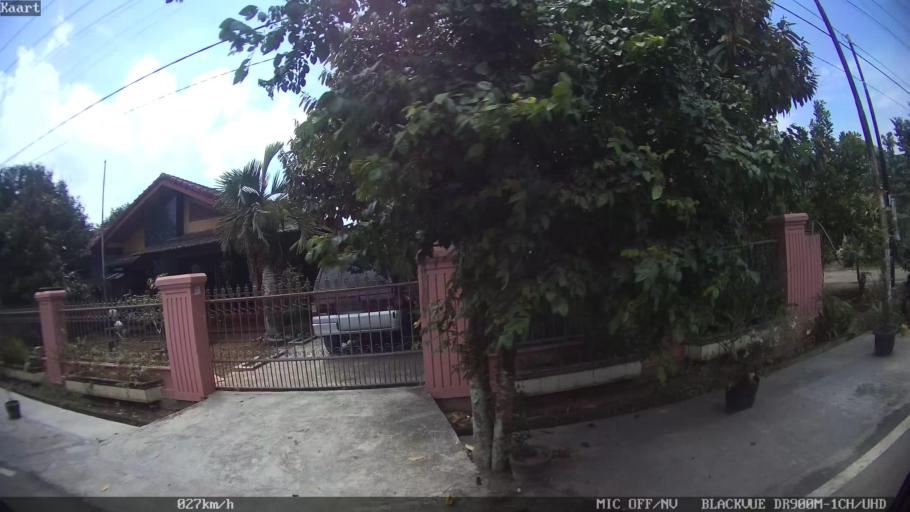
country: ID
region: Lampung
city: Kedaton
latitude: -5.3711
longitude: 105.3016
